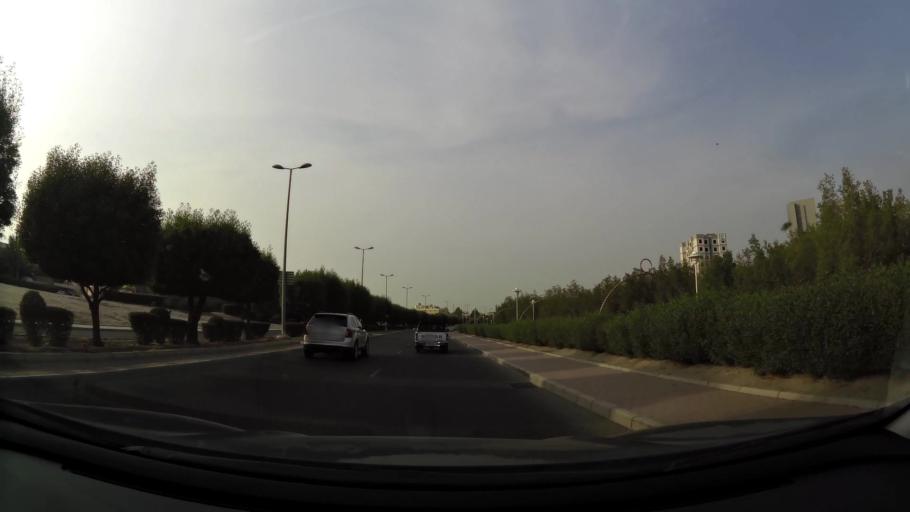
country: KW
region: Mubarak al Kabir
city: Sabah as Salim
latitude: 29.2536
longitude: 48.0791
